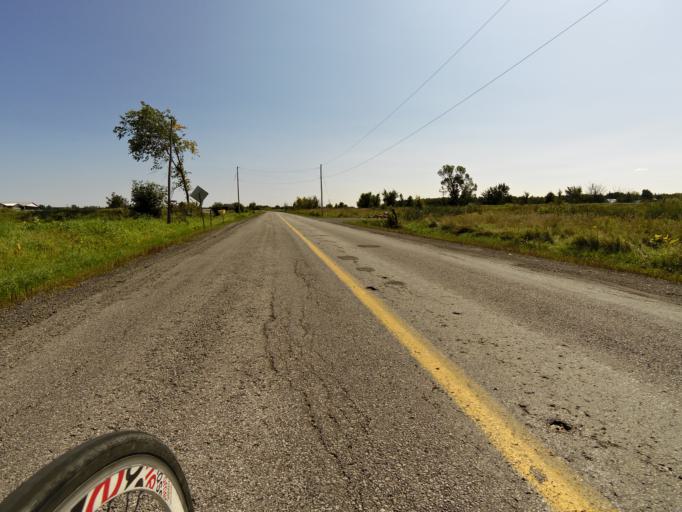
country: CA
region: Ontario
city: Arnprior
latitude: 45.4509
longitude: -76.0847
